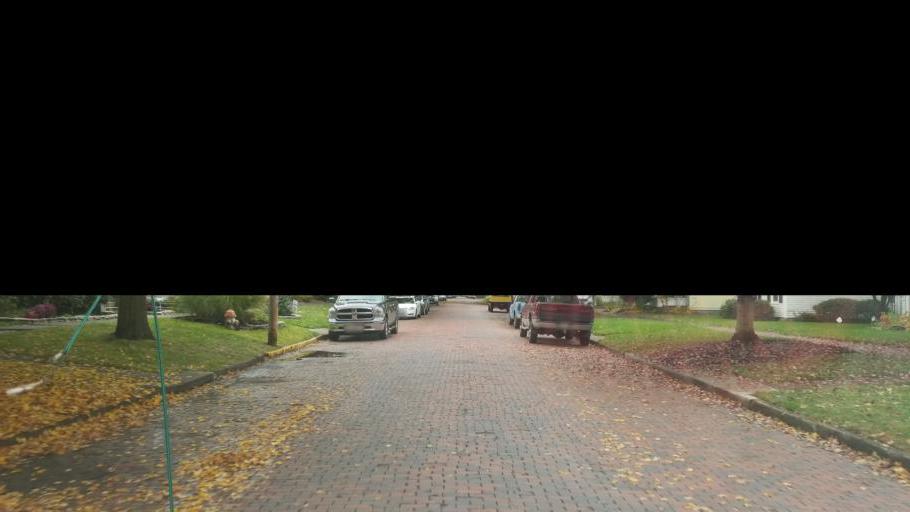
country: US
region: Ohio
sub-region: Washington County
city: Marietta
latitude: 39.4276
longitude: -81.4587
